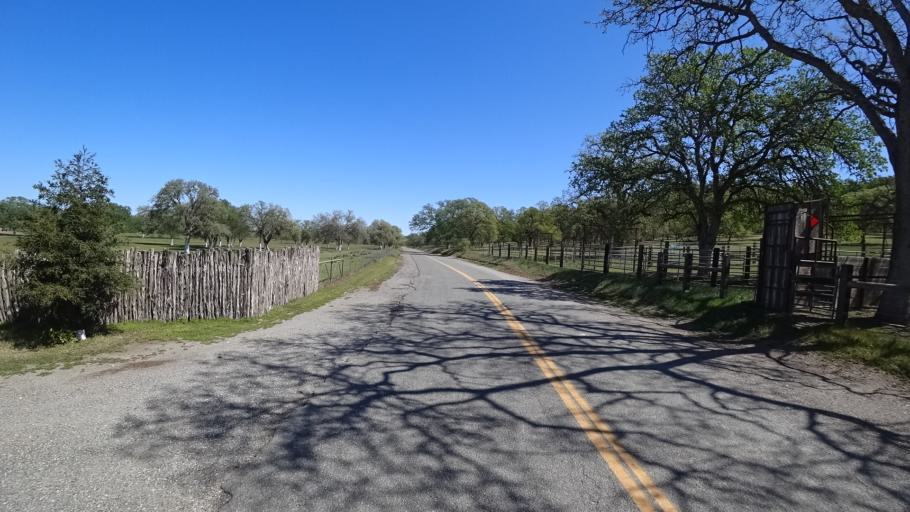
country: US
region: California
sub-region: Glenn County
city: Orland
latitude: 39.7317
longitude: -122.4042
